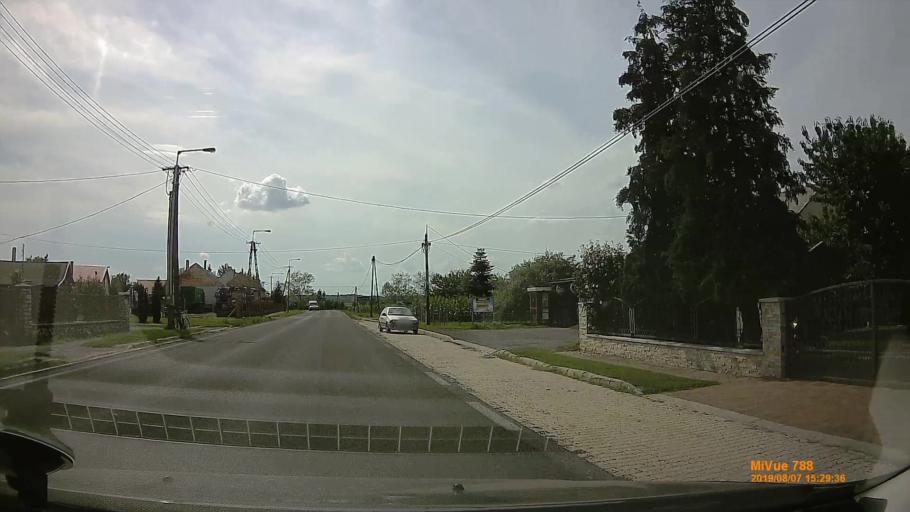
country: HU
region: Vas
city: Vep
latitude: 47.2831
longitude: 16.7758
